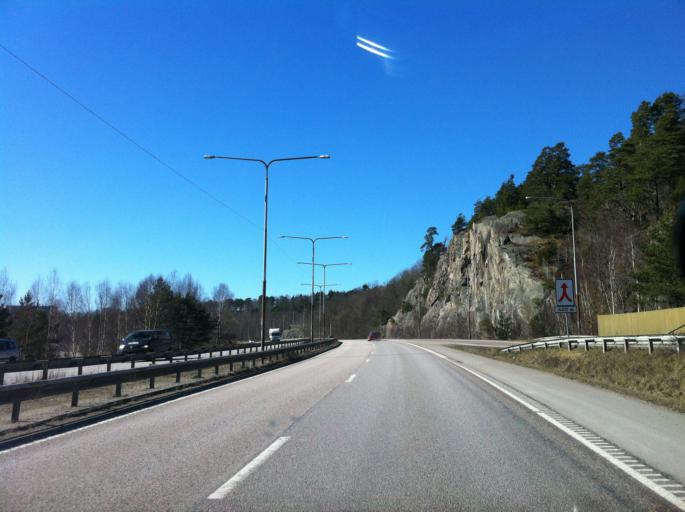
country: SE
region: Vaestra Goetaland
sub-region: Vanersborgs Kommun
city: Vanersborg
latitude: 58.3529
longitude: 12.3145
